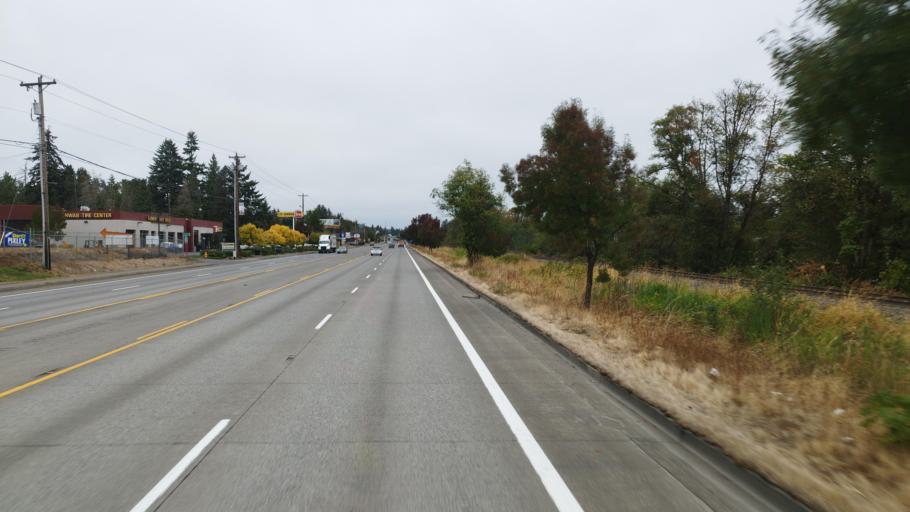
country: US
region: Oregon
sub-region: Columbia County
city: Warren
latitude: 45.8421
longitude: -122.8357
